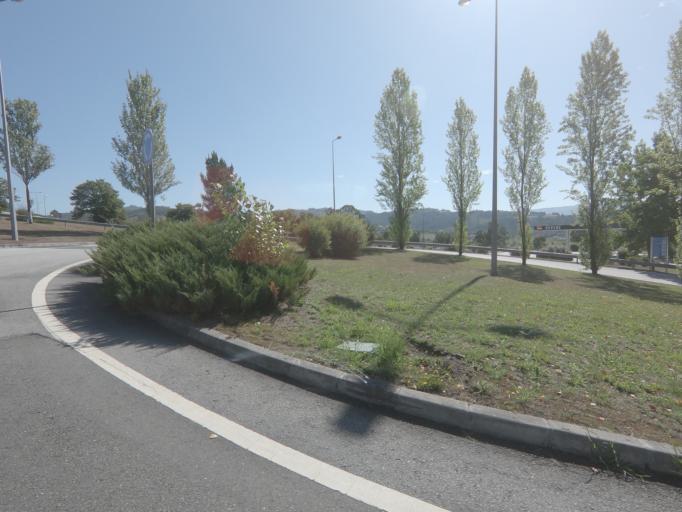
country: PT
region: Porto
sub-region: Marco de Canaveses
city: Marco de Canavezes
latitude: 41.2336
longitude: -8.1798
